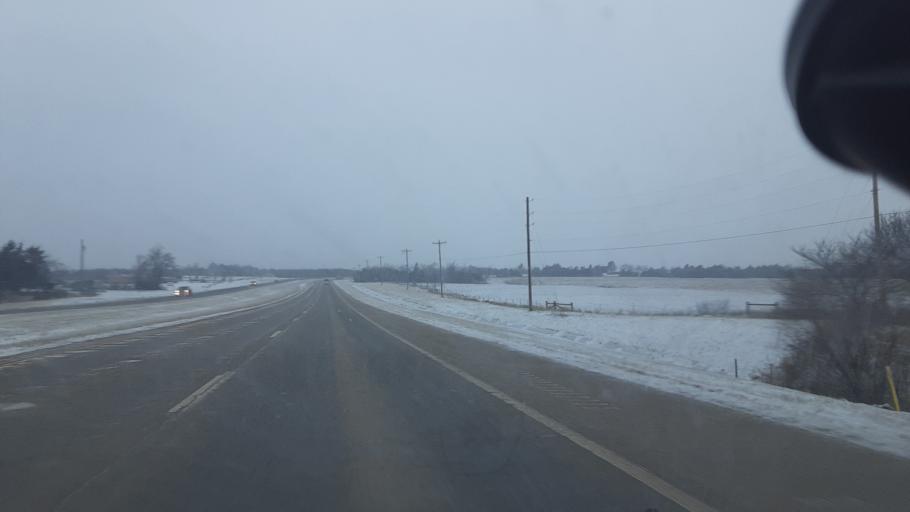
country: US
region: Oklahoma
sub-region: Logan County
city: Guthrie
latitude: 35.8901
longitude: -97.3658
